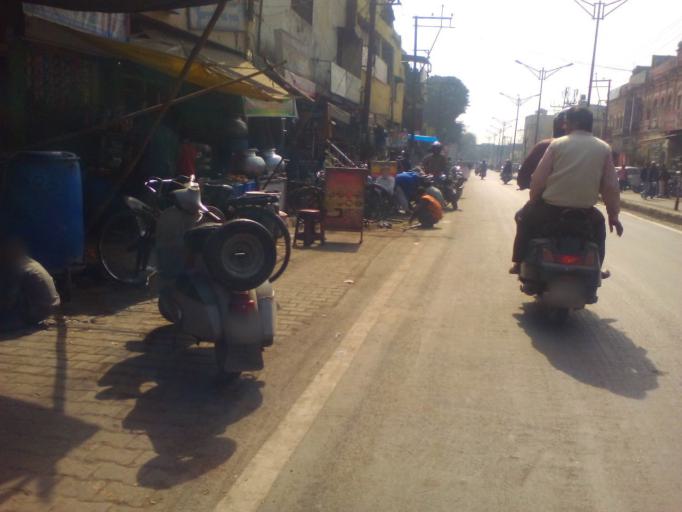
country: IN
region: Uttarakhand
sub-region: Dehradun
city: Dehradun
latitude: 30.3198
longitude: 78.0403
